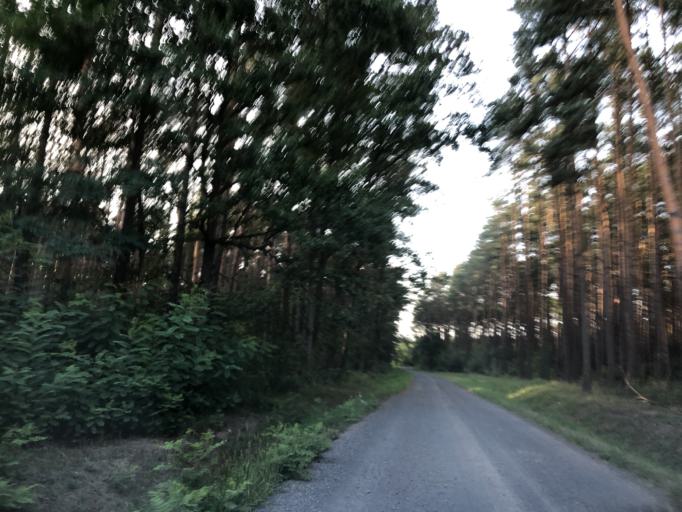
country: PL
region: Lubusz
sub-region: Powiat swiebodzinski
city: Zbaszynek
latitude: 52.2333
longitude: 15.7914
